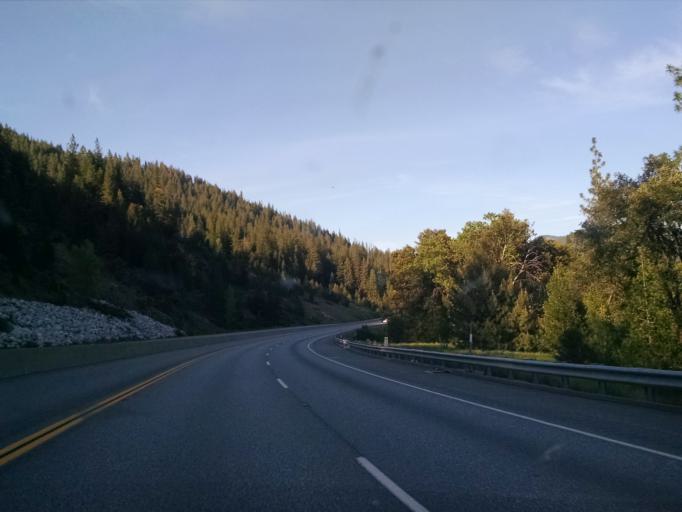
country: US
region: California
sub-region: Siskiyou County
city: Dunsmuir
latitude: 41.0425
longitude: -122.3949
